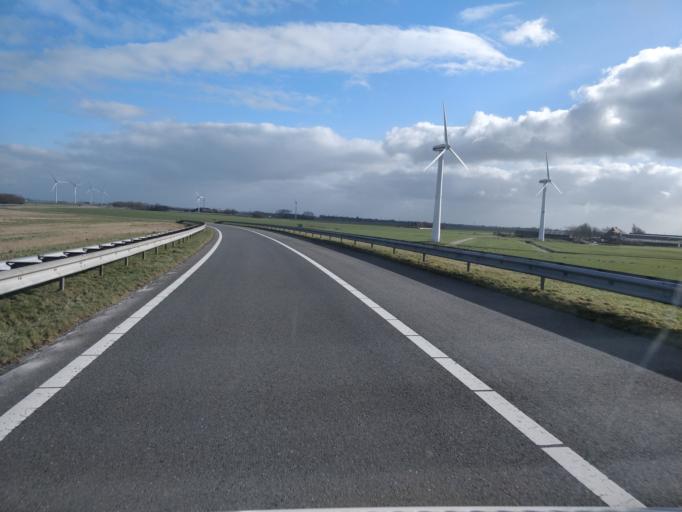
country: NL
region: Friesland
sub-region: Sudwest Fryslan
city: Makkum
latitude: 53.0965
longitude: 5.3938
